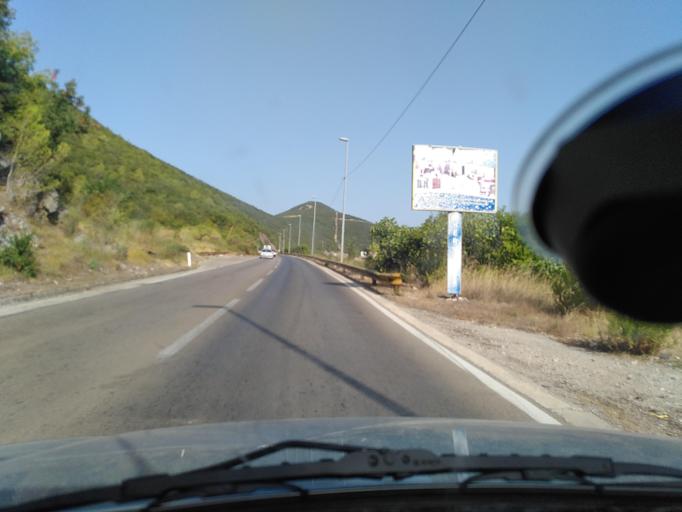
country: ME
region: Ulcinj
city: Ulcinj
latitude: 41.9469
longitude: 19.2027
